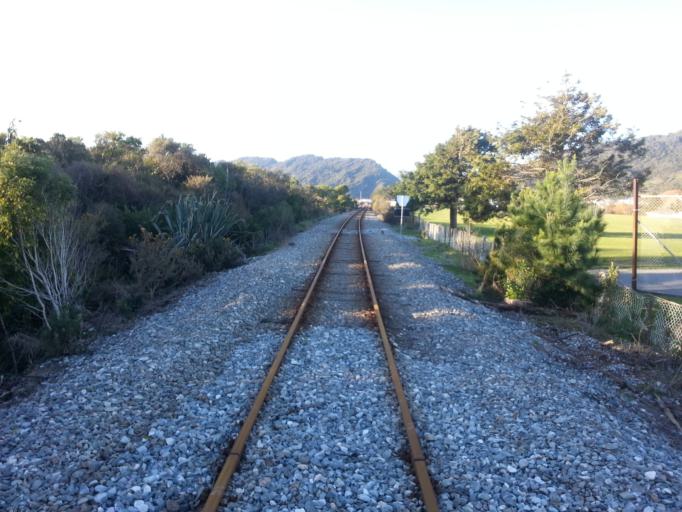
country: NZ
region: West Coast
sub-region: Grey District
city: Greymouth
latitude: -42.4590
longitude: 171.1979
